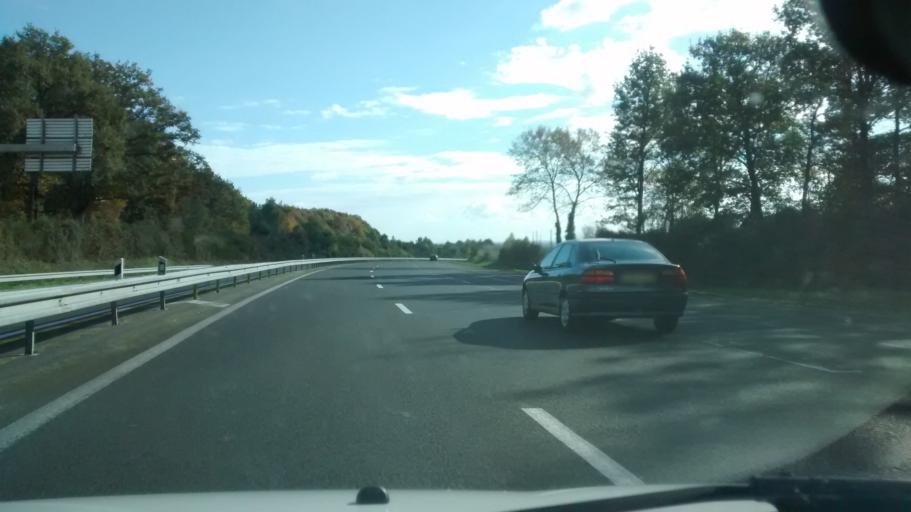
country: FR
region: Pays de la Loire
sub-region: Departement de Maine-et-Loire
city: Combree
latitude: 47.7142
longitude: -1.0084
